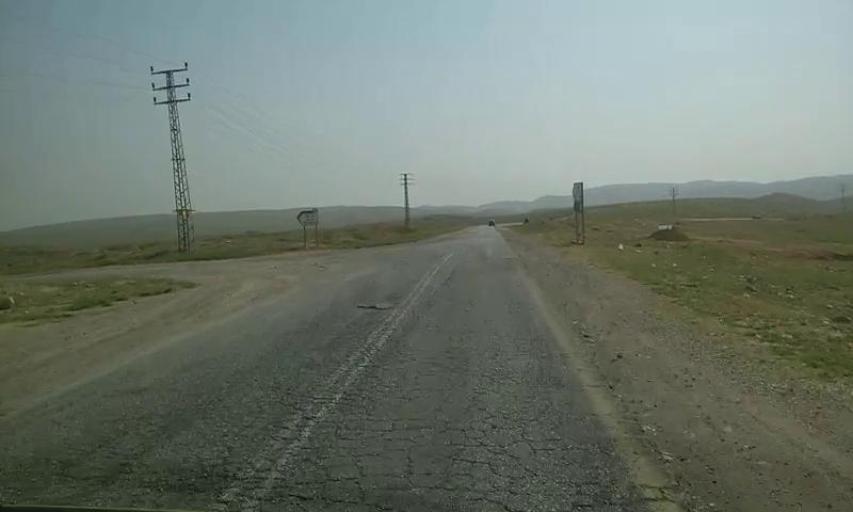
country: PS
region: West Bank
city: An Nuway`imah
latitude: 31.9215
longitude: 35.4159
